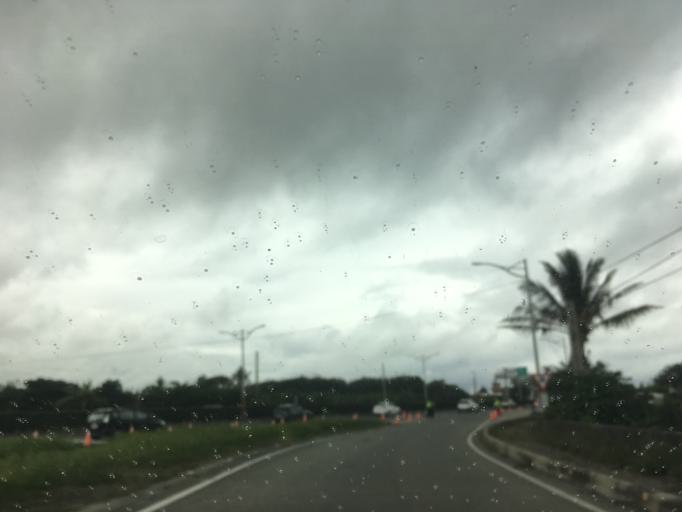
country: TW
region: Taiwan
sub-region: Taitung
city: Taitung
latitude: 22.7766
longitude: 121.1749
